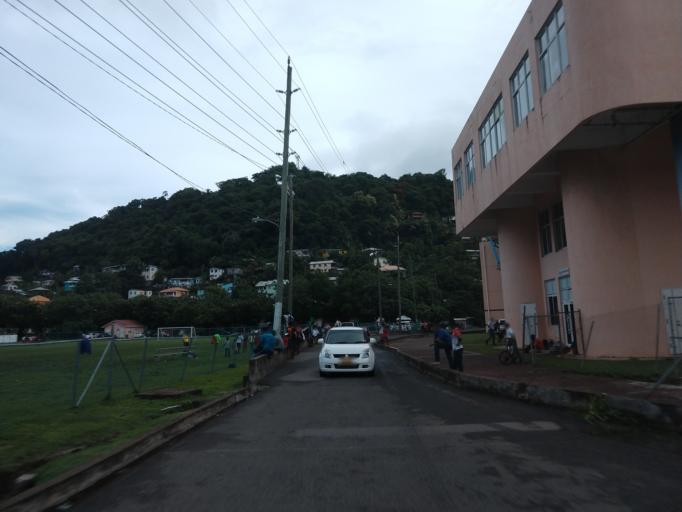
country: GD
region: Saint George
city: Saint George's
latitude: 12.0593
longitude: -61.7512
